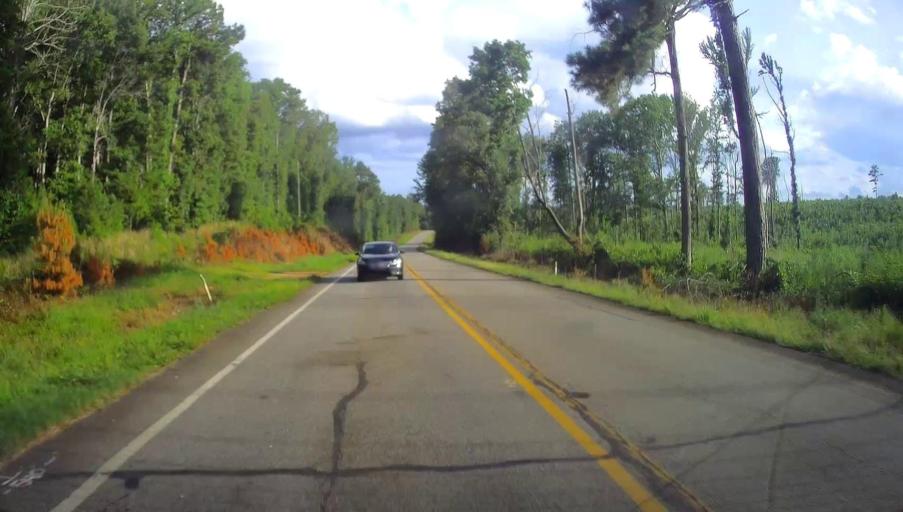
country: US
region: Georgia
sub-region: Crawford County
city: Knoxville
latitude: 32.8726
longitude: -83.9944
